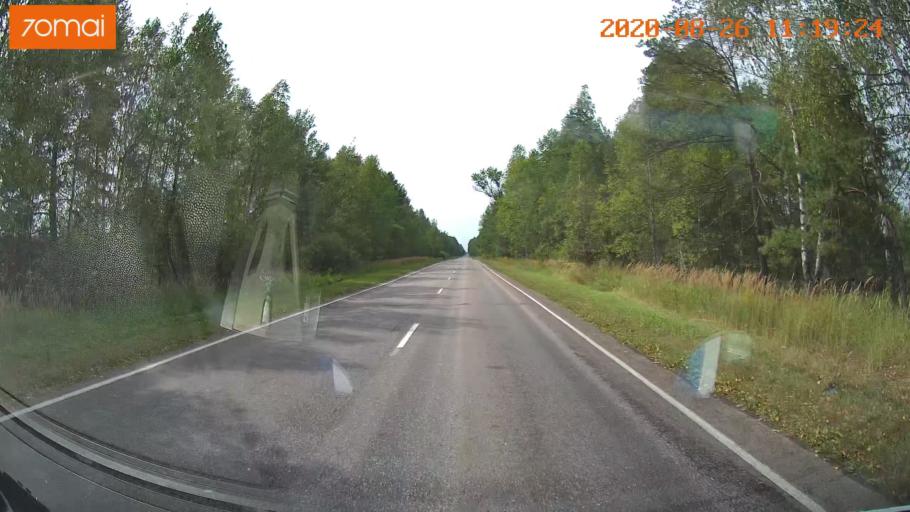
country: RU
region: Rjazan
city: Shilovo
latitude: 54.3996
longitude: 41.0805
